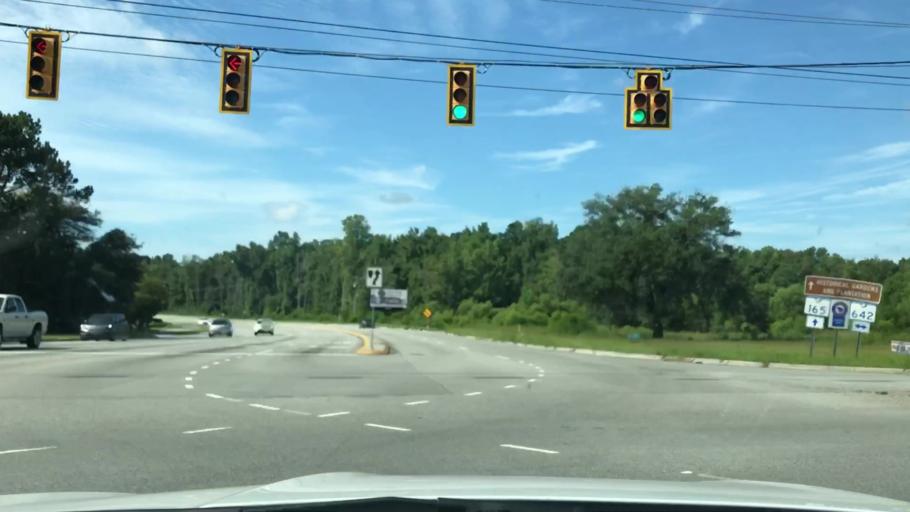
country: US
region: South Carolina
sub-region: Dorchester County
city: Centerville
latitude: 32.9677
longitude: -80.2014
